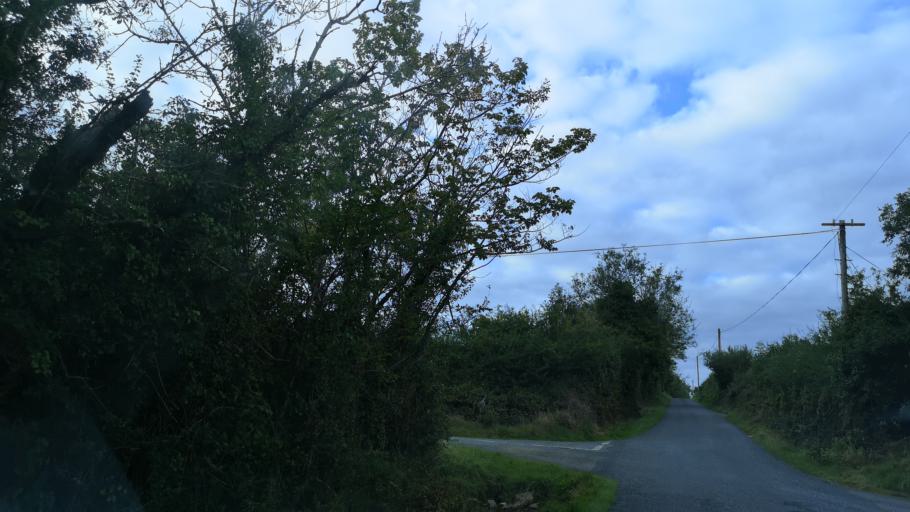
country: IE
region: Connaught
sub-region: County Galway
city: Loughrea
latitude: 53.1490
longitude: -8.5164
